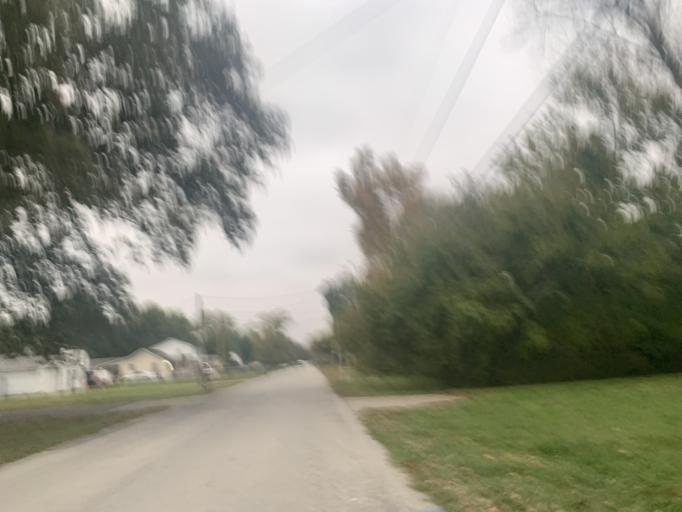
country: US
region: Kentucky
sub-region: Jefferson County
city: Saint Dennis
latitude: 38.2055
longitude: -85.8528
